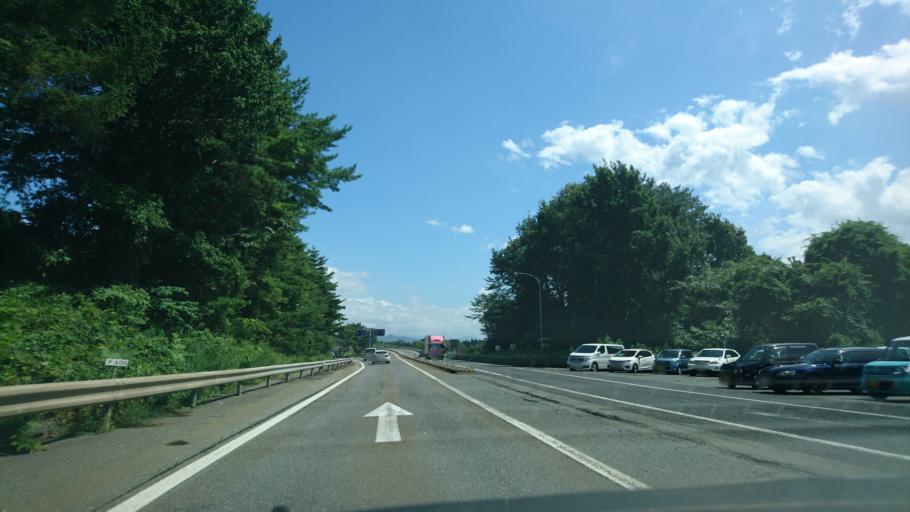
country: JP
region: Iwate
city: Morioka-shi
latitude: 39.7971
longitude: 141.1207
